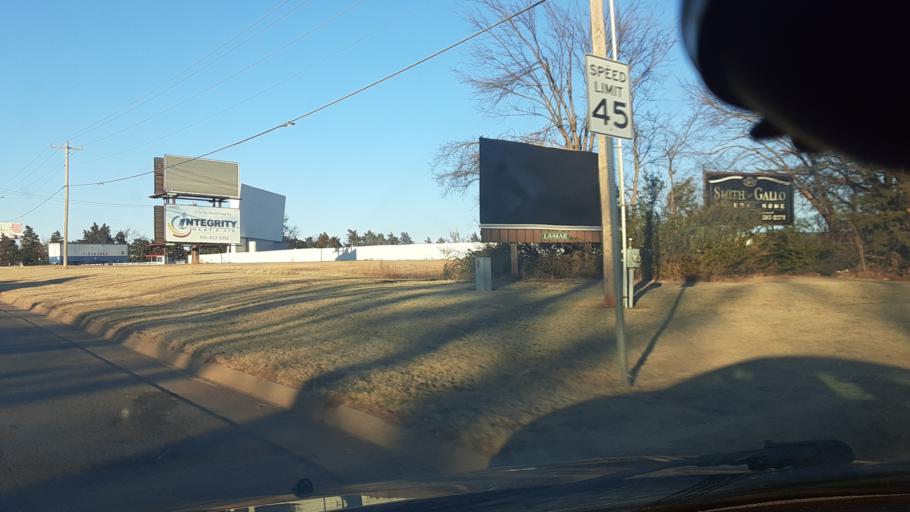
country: US
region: Oklahoma
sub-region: Logan County
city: Guthrie
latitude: 35.8525
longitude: -97.4254
